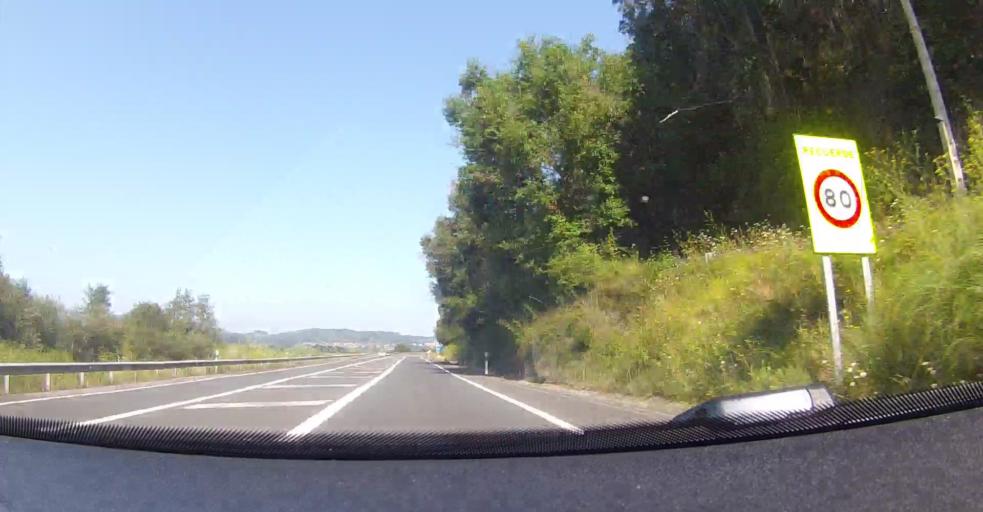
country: ES
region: Cantabria
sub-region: Provincia de Cantabria
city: Limpias
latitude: 43.3801
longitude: -3.4350
